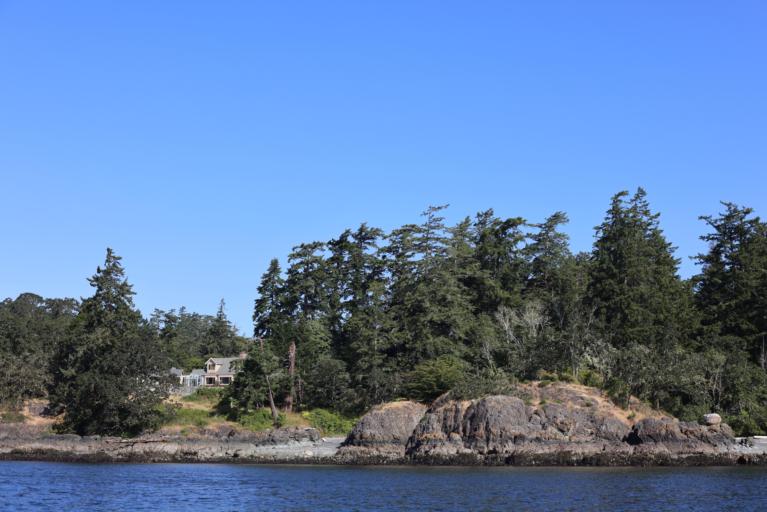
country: CA
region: British Columbia
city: Metchosin
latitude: 48.3565
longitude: -123.5393
